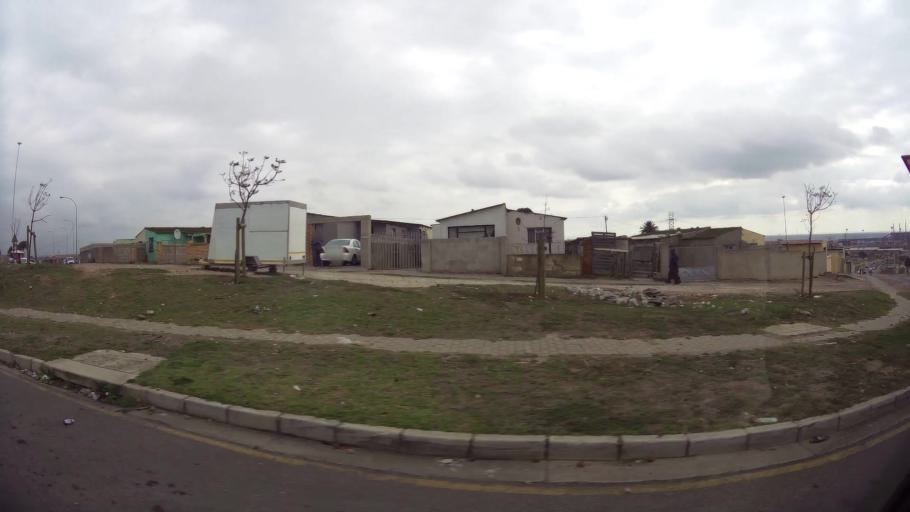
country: ZA
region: Eastern Cape
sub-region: Nelson Mandela Bay Metropolitan Municipality
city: Port Elizabeth
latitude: -33.8913
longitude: 25.5951
